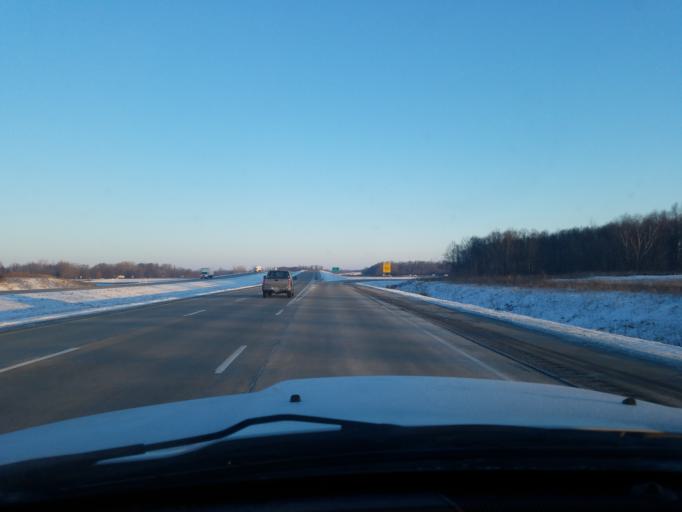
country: US
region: Indiana
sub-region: Marshall County
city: Plymouth
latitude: 41.4450
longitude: -86.2923
